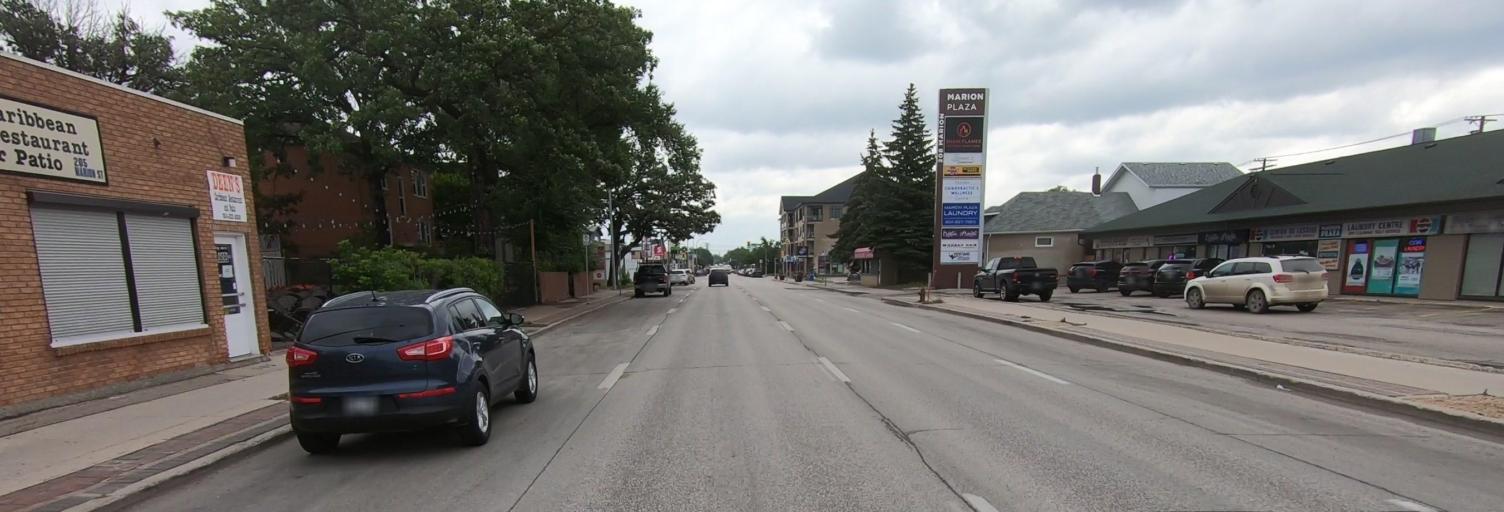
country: CA
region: Manitoba
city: Winnipeg
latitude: 49.8816
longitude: -97.1192
